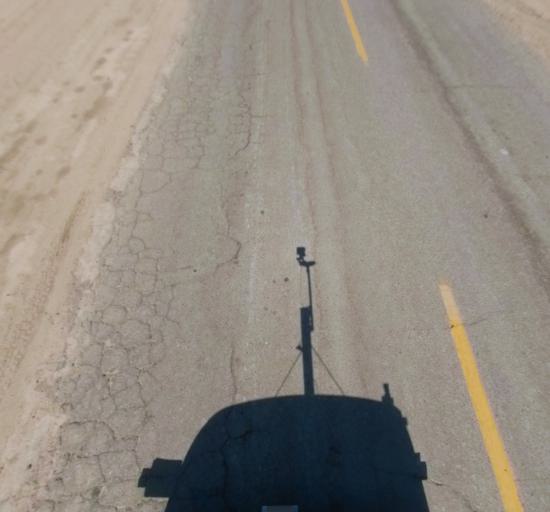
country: US
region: California
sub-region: Madera County
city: Parkwood
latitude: 36.8802
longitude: -120.1390
